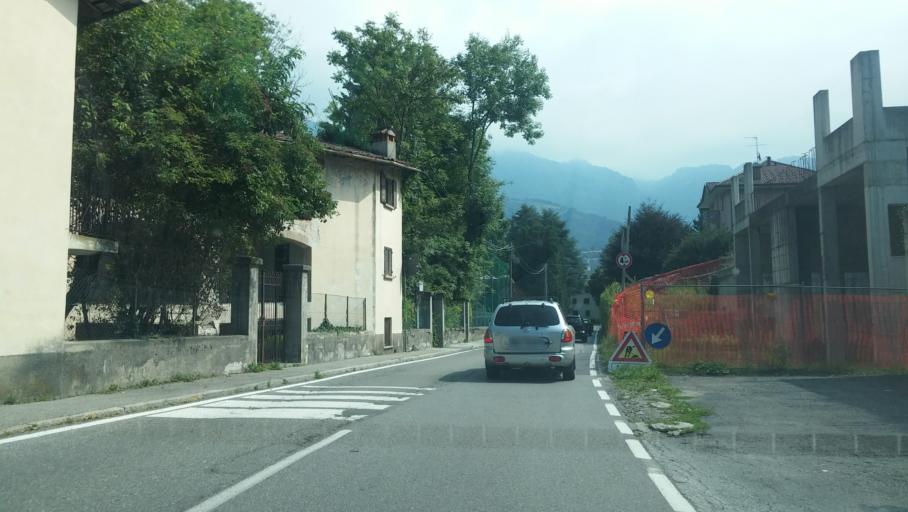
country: IT
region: Lombardy
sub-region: Provincia di Lecco
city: Cremeno
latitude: 45.9278
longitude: 9.4604
